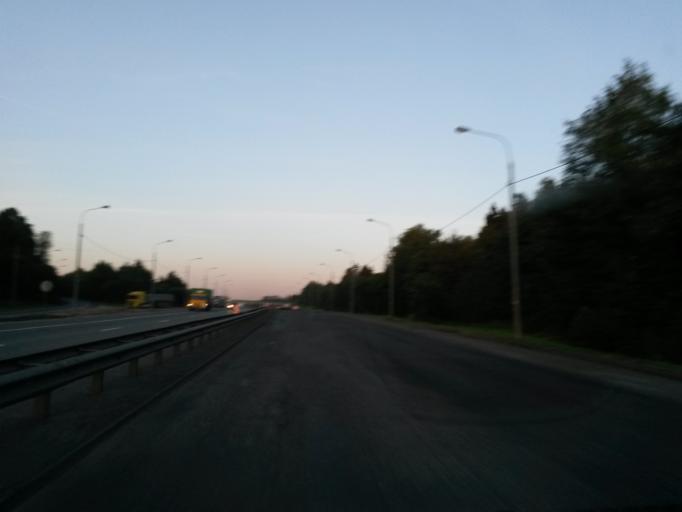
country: RU
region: Moskovskaya
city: Sergiyev Posad
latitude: 56.2914
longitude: 38.2188
